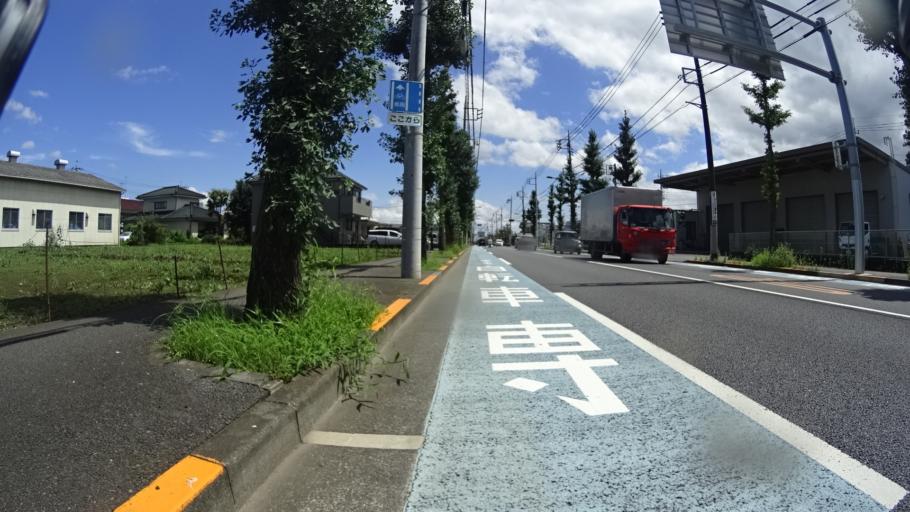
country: JP
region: Tokyo
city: Fussa
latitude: 35.7723
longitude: 139.3029
